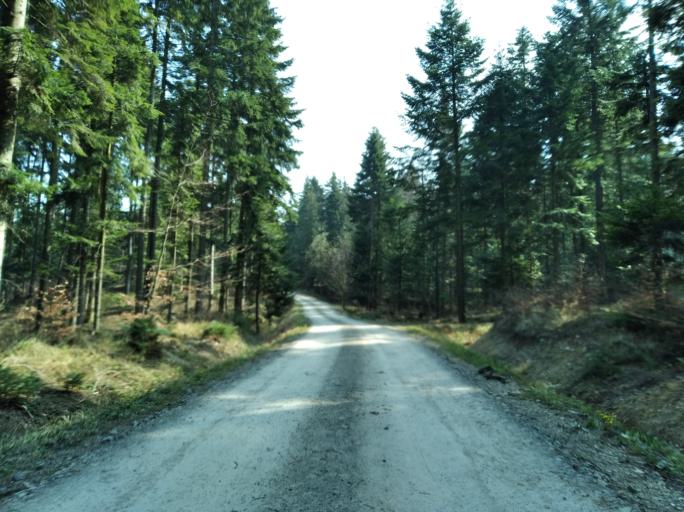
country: PL
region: Subcarpathian Voivodeship
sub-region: Powiat strzyzowski
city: Wysoka Strzyzowska
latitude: 49.8284
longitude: 21.7840
